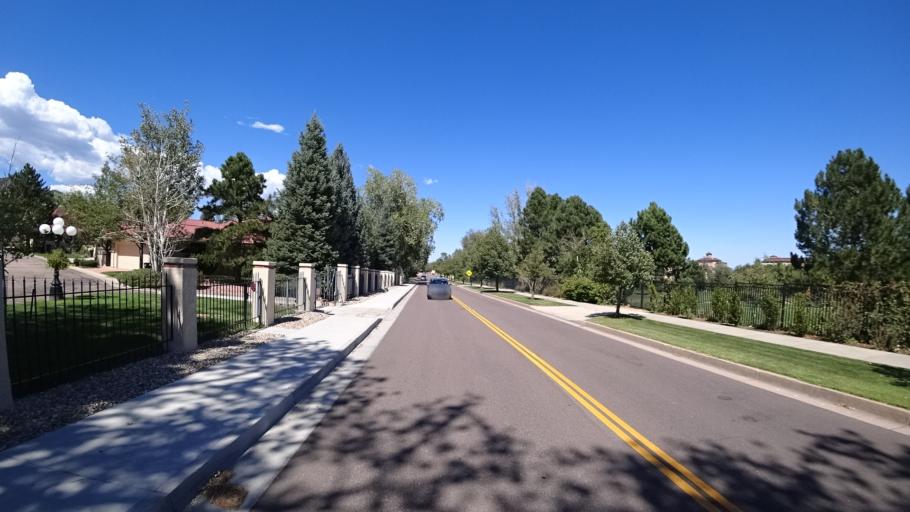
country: US
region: Colorado
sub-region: El Paso County
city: Colorado Springs
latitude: 38.7873
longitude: -104.8548
